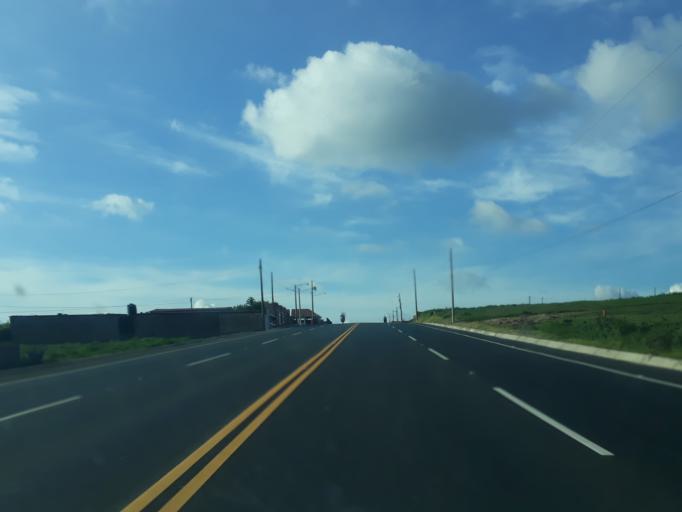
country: NI
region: Managua
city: El Crucero
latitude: 11.9535
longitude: -86.3017
